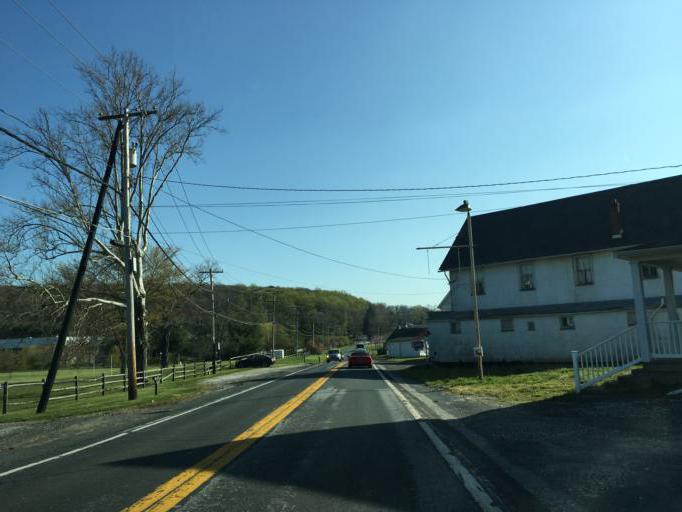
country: US
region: Maryland
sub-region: Baltimore County
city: Perry Hall
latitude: 39.4584
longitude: -76.4923
